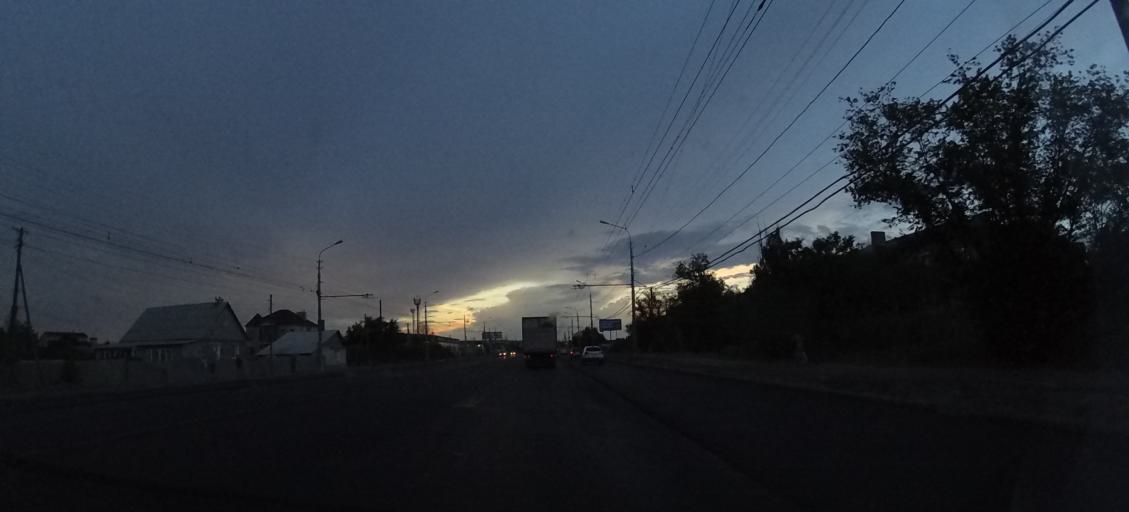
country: RU
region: Volgograd
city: Volgograd
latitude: 48.5866
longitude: 44.4216
